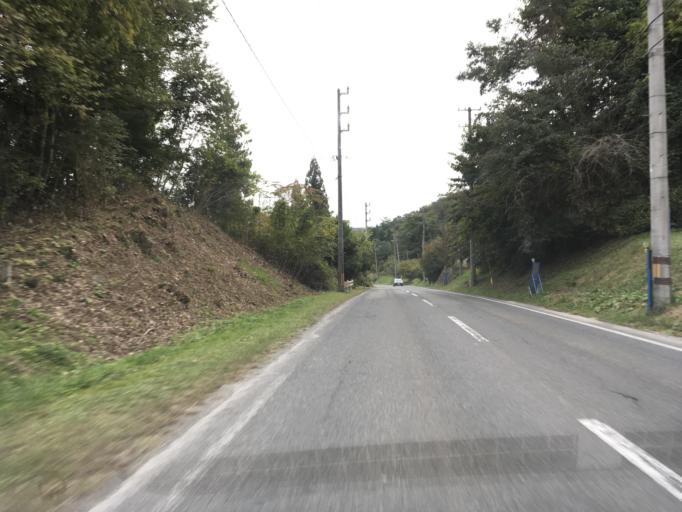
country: JP
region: Iwate
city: Ichinoseki
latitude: 39.0087
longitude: 141.2856
